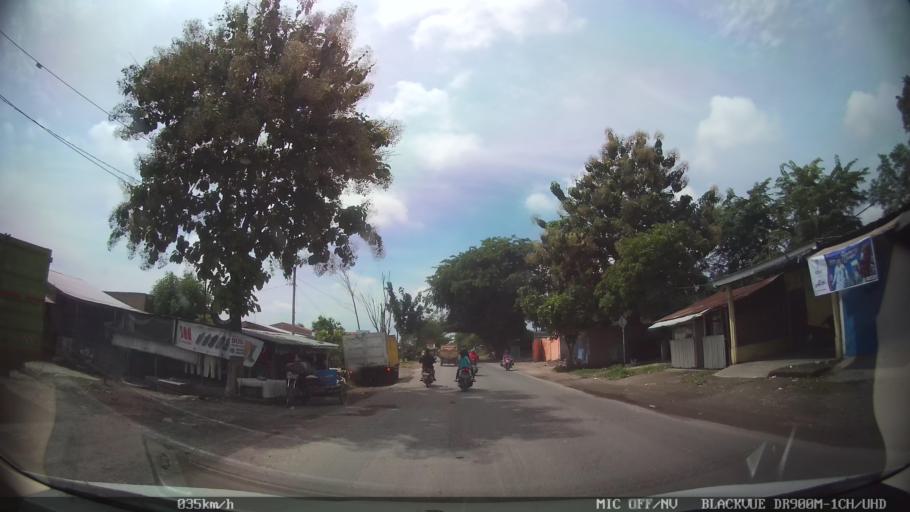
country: ID
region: North Sumatra
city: Medan
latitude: 3.6489
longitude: 98.7086
